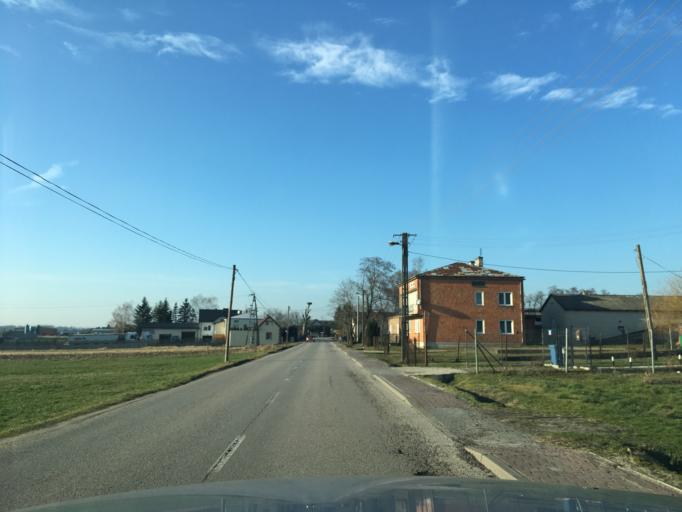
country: PL
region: Masovian Voivodeship
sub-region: Powiat pruszkowski
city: Nadarzyn
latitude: 52.0384
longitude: 20.8181
